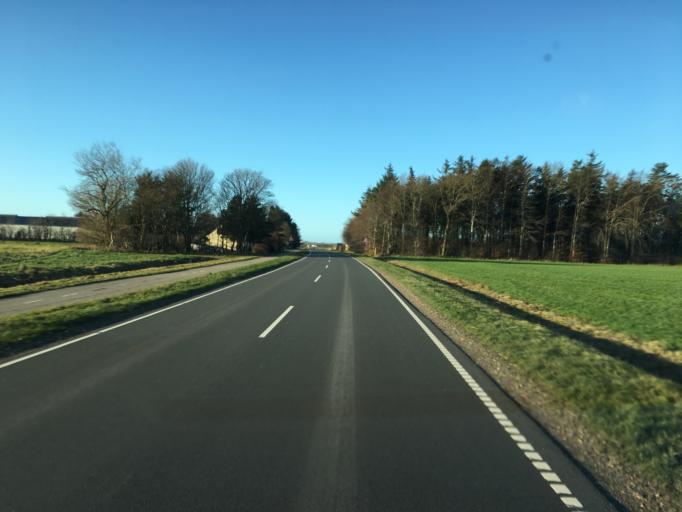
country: DK
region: North Denmark
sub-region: Hjorring Kommune
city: Vra
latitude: 57.3562
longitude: 9.8870
